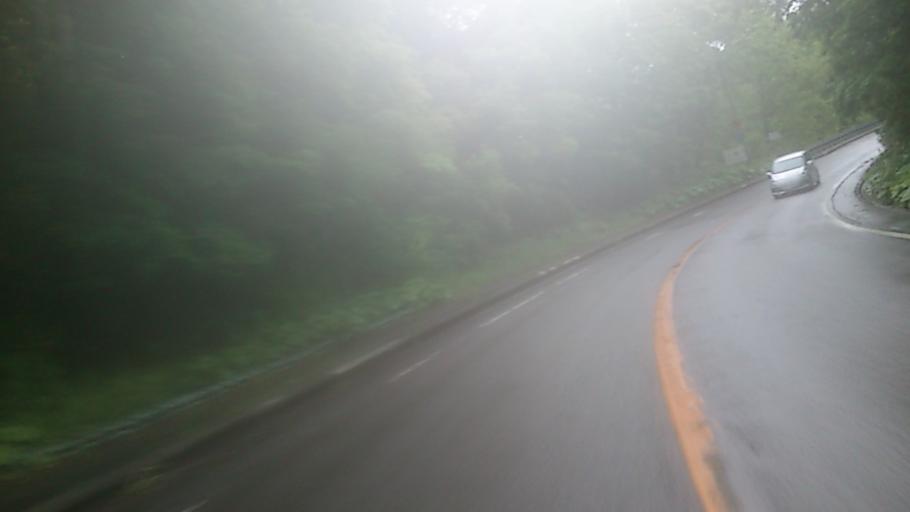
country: JP
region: Hokkaido
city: Shiraoi
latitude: 42.7696
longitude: 141.4144
